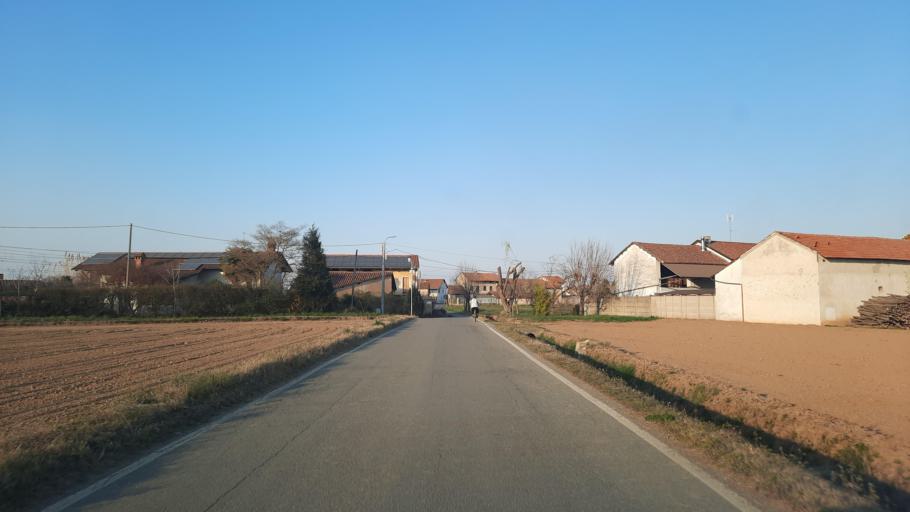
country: IT
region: Piedmont
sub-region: Provincia di Vercelli
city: Bianze
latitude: 45.3061
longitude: 8.1110
